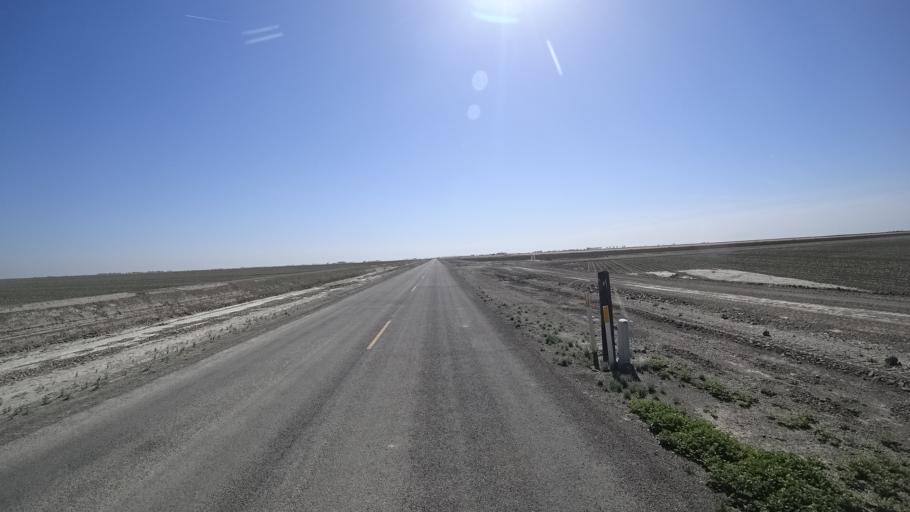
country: US
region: California
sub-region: Tulare County
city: Alpaugh
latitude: 35.8914
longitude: -119.5480
